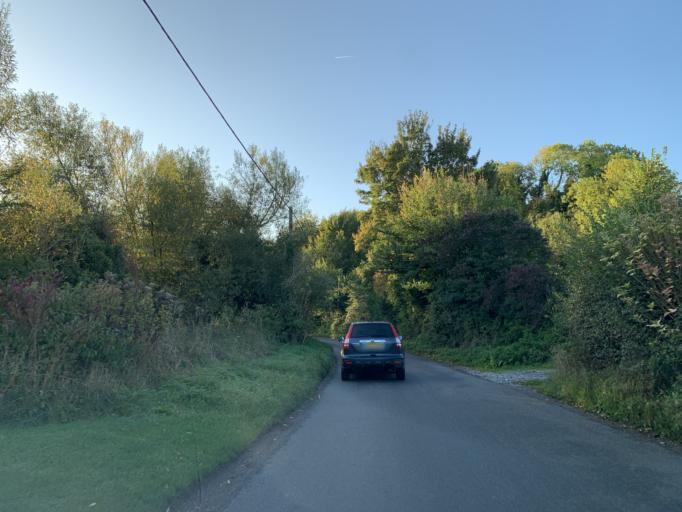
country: GB
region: England
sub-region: Wiltshire
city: Woodford
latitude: 51.1215
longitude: -1.8295
